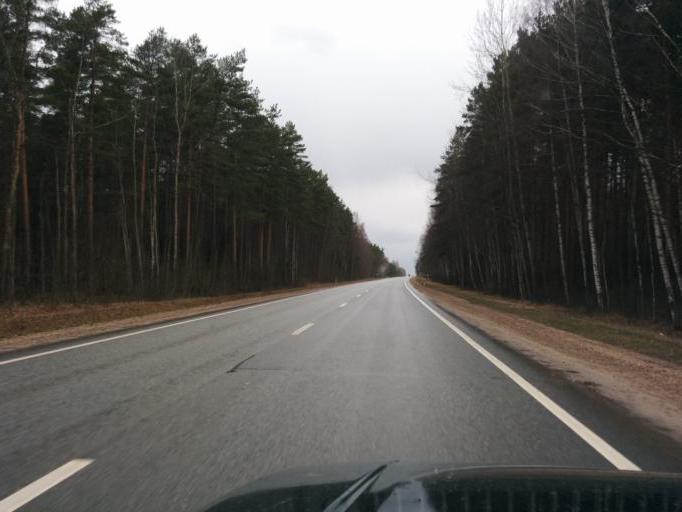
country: LV
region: Marupe
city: Marupe
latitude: 56.8421
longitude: 24.0218
